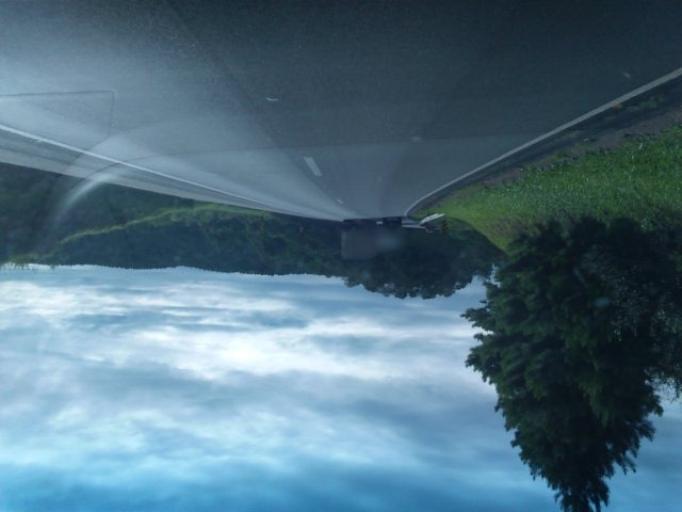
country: BR
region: Parana
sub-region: Campina Grande Do Sul
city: Campina Grande do Sul
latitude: -25.1098
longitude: -48.8523
